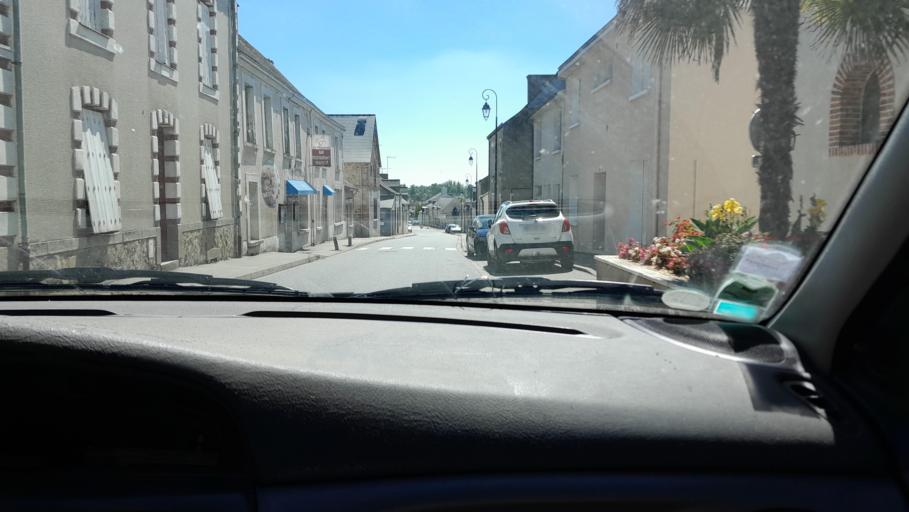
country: FR
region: Pays de la Loire
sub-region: Departement de la Mayenne
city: Congrier
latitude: 47.8412
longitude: -1.1377
